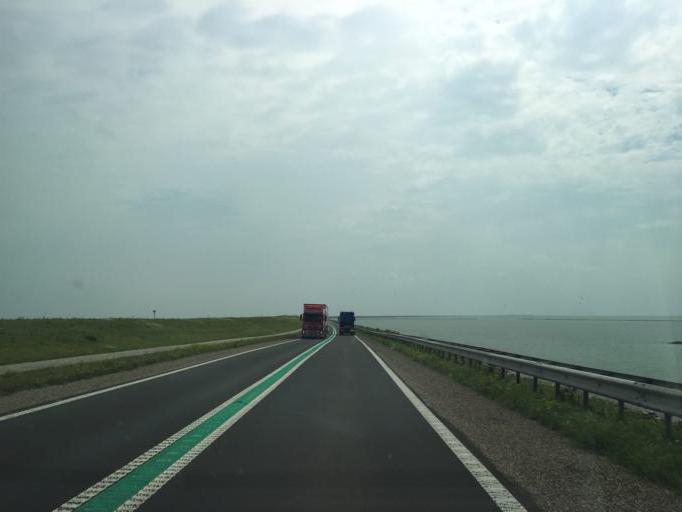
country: NL
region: North Holland
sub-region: Gemeente Enkhuizen
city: Enkhuizen
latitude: 52.6833
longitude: 5.3317
